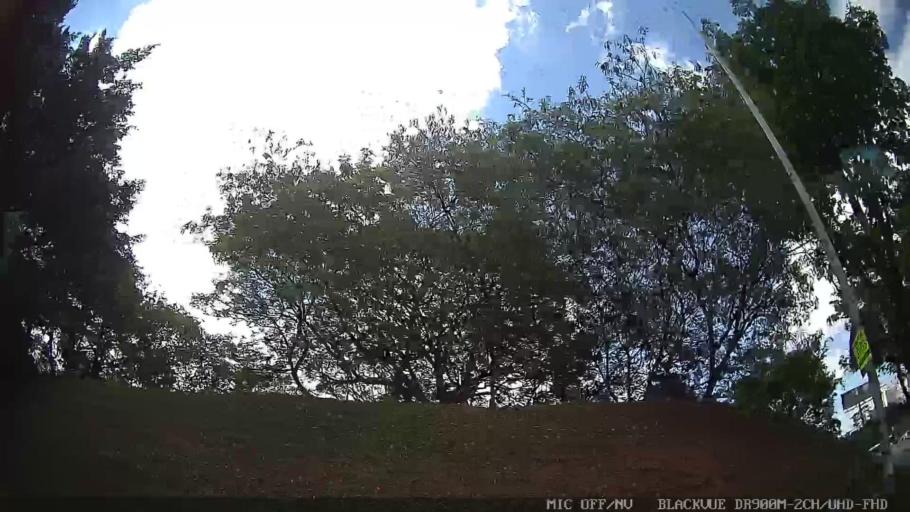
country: BR
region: Sao Paulo
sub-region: Sao Caetano Do Sul
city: Sao Caetano do Sul
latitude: -23.6486
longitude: -46.5795
